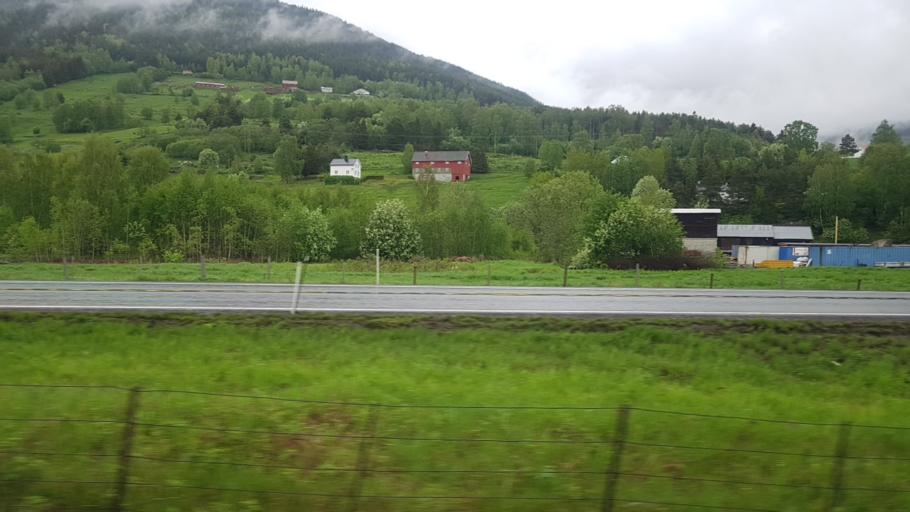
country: NO
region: Oppland
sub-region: Sor-Fron
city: Hundorp
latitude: 61.5466
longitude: 10.0299
